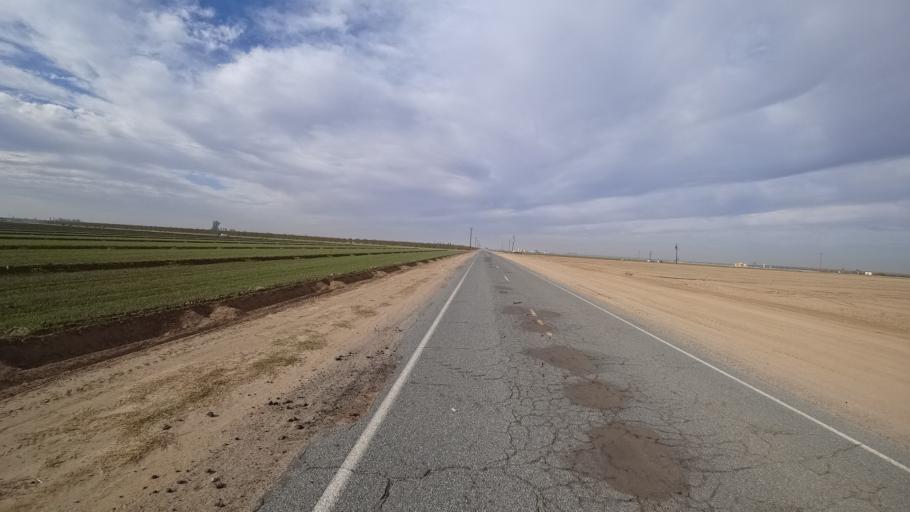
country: US
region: California
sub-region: Kern County
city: Rosedale
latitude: 35.4124
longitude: -119.1699
